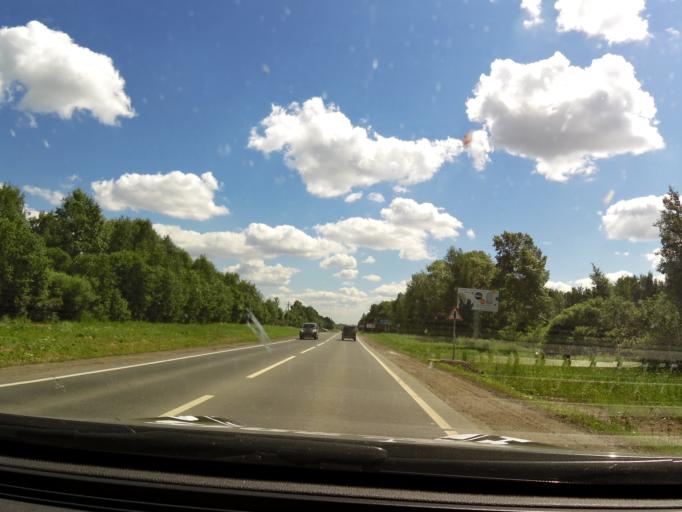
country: RU
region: Vologda
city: Molochnoye
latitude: 59.2568
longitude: 39.7564
